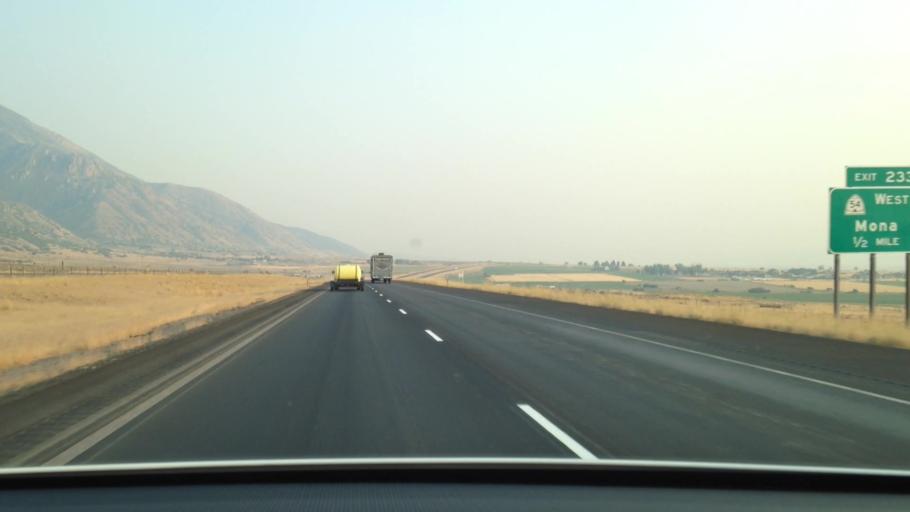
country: US
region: Utah
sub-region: Juab County
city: Mona
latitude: 39.8321
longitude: -111.8348
